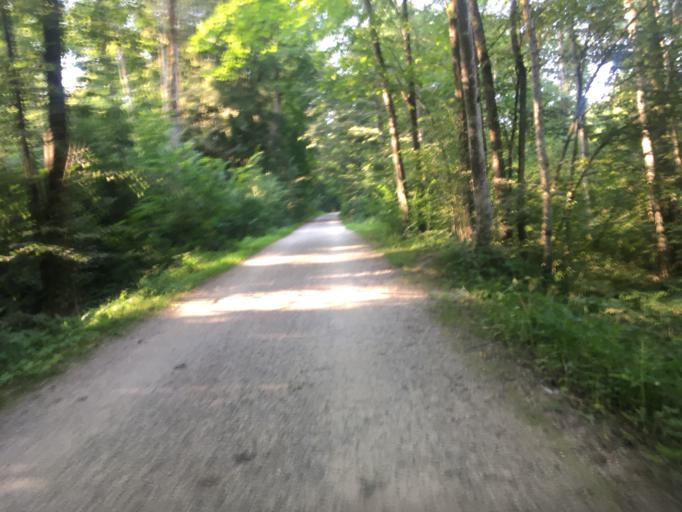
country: CH
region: Bern
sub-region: Emmental District
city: Oberburg
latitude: 47.0423
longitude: 7.6326
